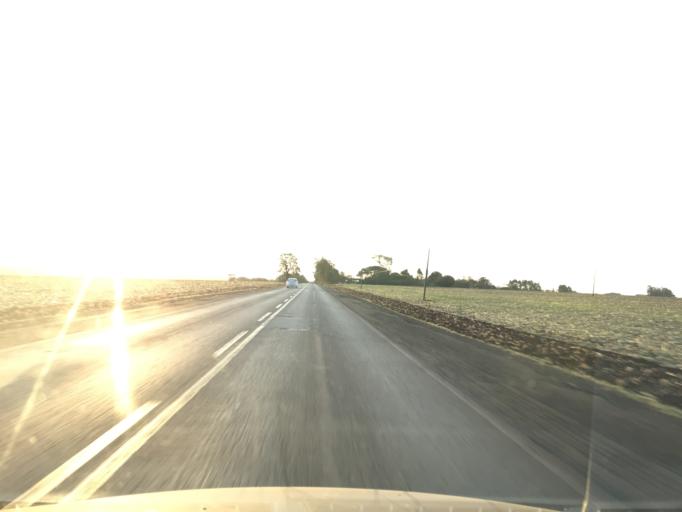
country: BR
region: Parana
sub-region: Toledo
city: Toledo
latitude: -24.4996
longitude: -53.7883
